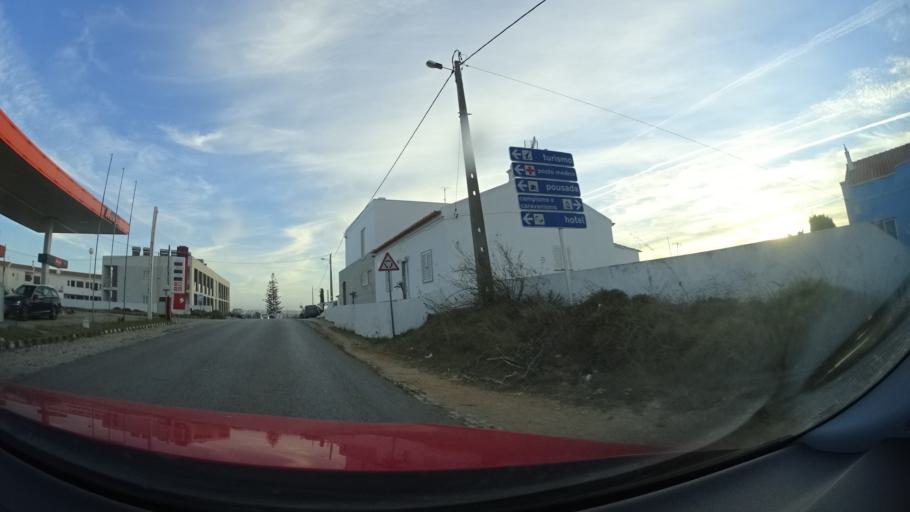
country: PT
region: Faro
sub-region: Vila do Bispo
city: Sagres
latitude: 37.0089
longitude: -8.9443
